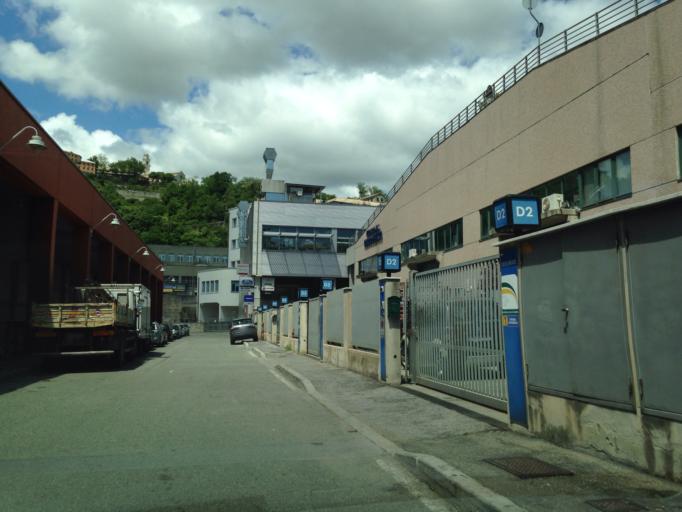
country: IT
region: Liguria
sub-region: Provincia di Genova
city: San Teodoro
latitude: 44.4226
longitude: 8.8825
